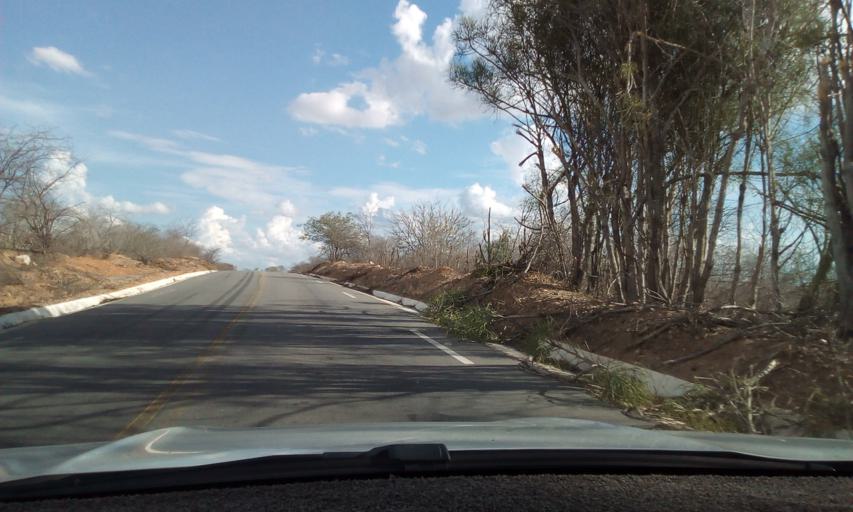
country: BR
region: Paraiba
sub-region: Soledade
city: Soledade
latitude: -6.9028
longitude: -36.3907
